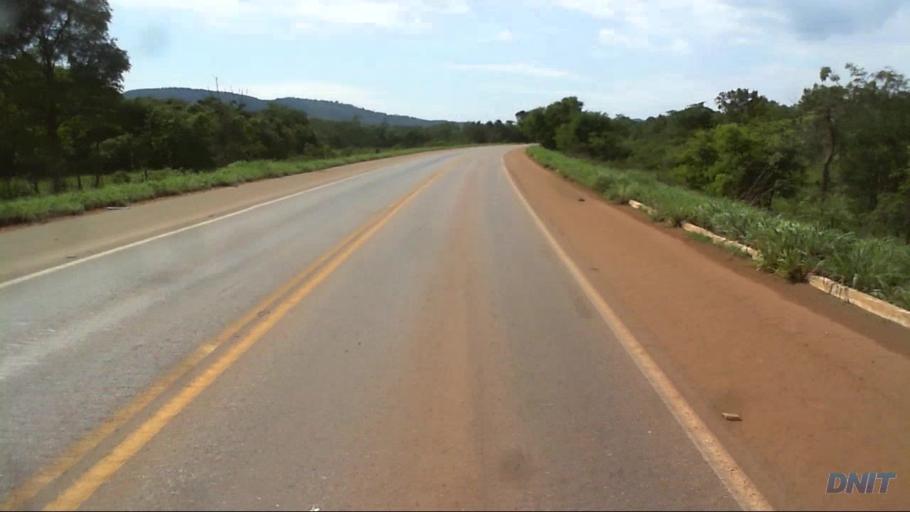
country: BR
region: Goias
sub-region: Barro Alto
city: Barro Alto
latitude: -15.0887
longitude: -48.8569
